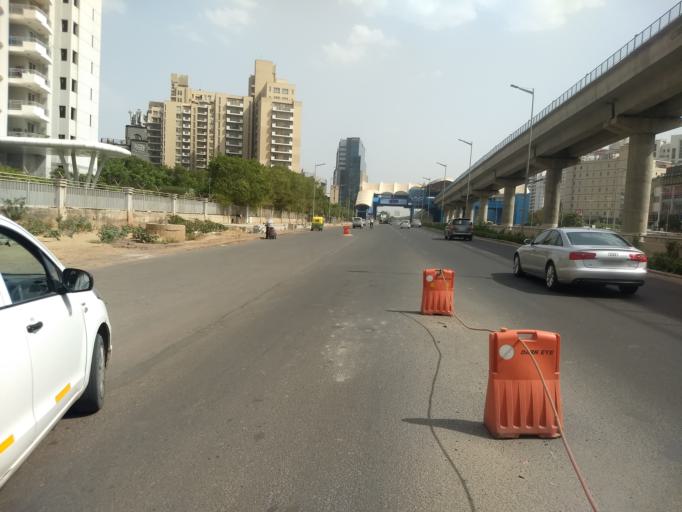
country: IN
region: Haryana
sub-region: Gurgaon
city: Gurgaon
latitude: 28.4490
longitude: 77.0999
